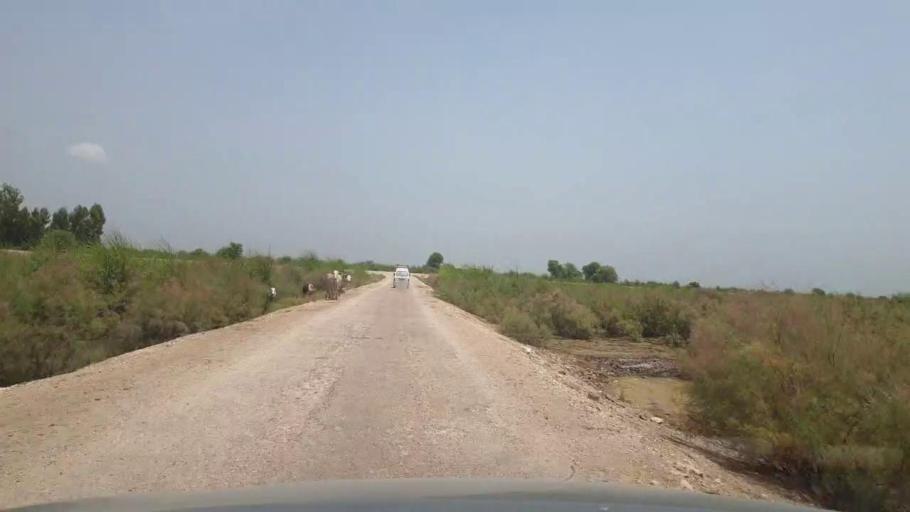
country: PK
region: Sindh
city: Garhi Yasin
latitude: 27.9563
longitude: 68.4414
